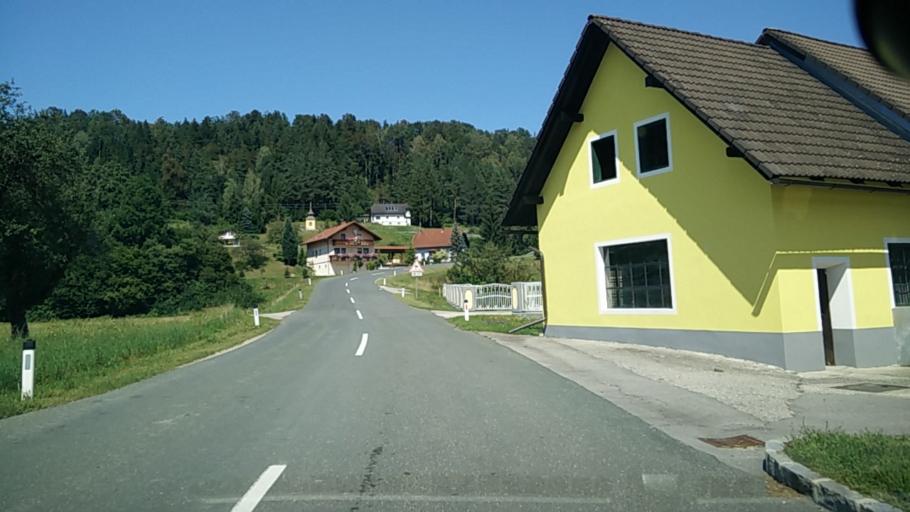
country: AT
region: Carinthia
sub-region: Politischer Bezirk Volkermarkt
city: Sittersdorf
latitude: 46.5586
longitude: 14.5637
